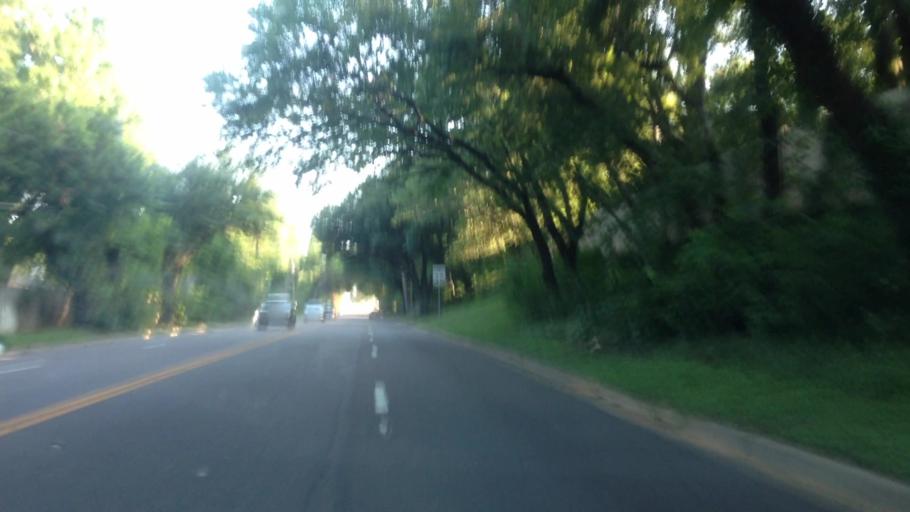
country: US
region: Texas
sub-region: Tarrant County
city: Pantego
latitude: 32.7203
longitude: -97.1689
